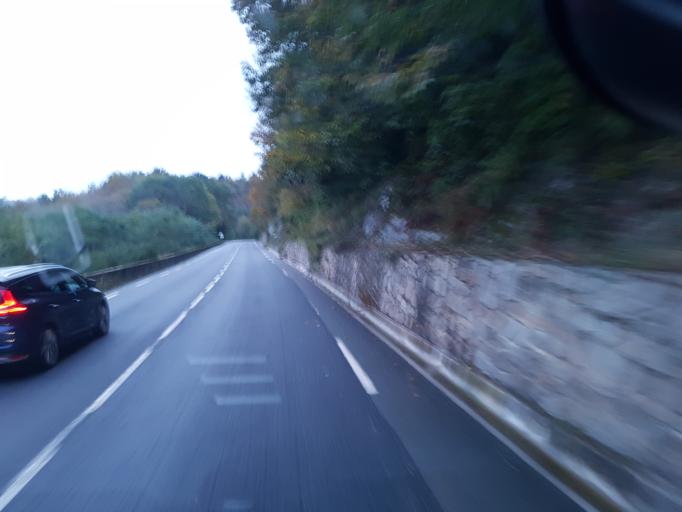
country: FR
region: Midi-Pyrenees
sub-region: Departement du Tarn
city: Mazamet
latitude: 43.4632
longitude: 2.3533
